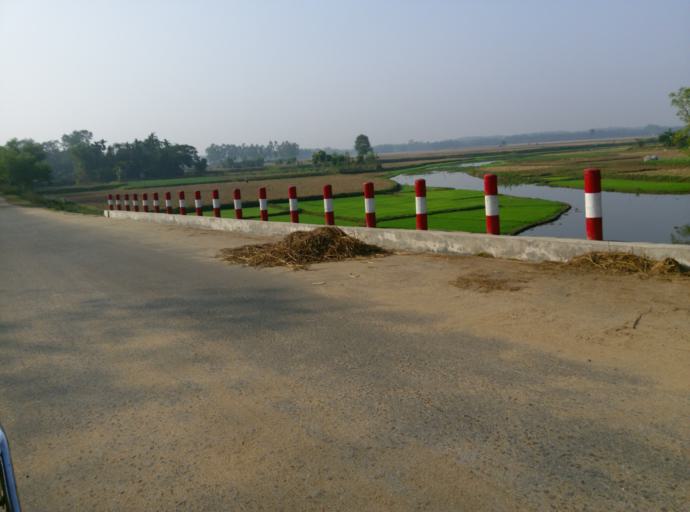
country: BD
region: Dhaka
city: Netrakona
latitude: 25.1498
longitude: 90.6593
